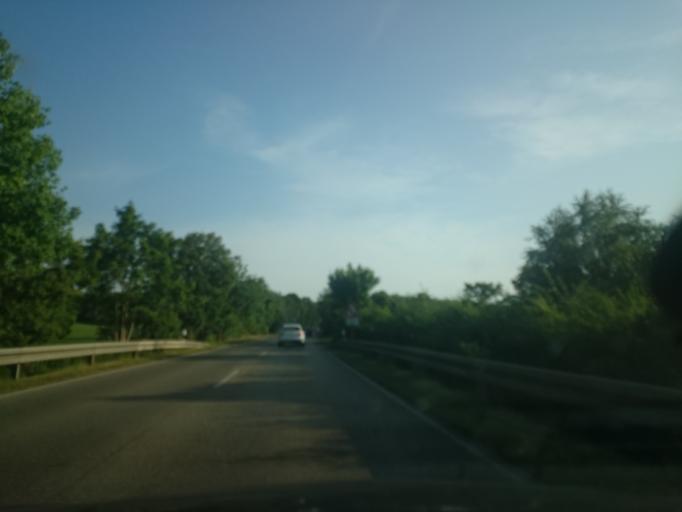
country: DE
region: Bavaria
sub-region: Upper Bavaria
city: Wessling
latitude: 48.0695
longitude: 11.2428
